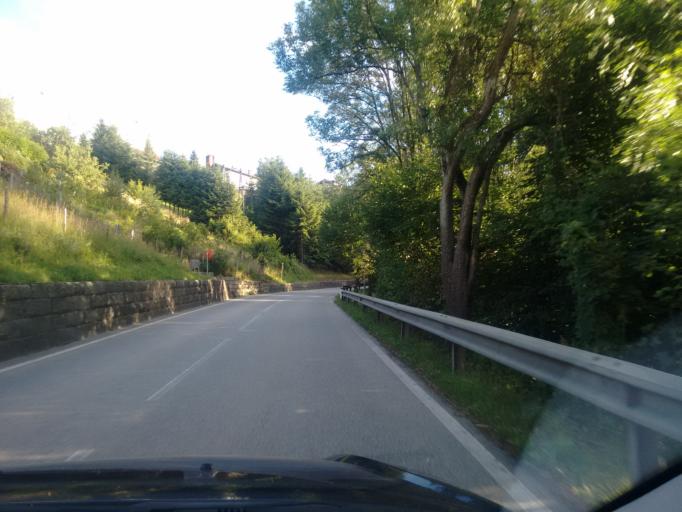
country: AT
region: Upper Austria
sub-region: Politischer Bezirk Urfahr-Umgebung
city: Gramastetten
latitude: 48.3836
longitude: 14.1941
